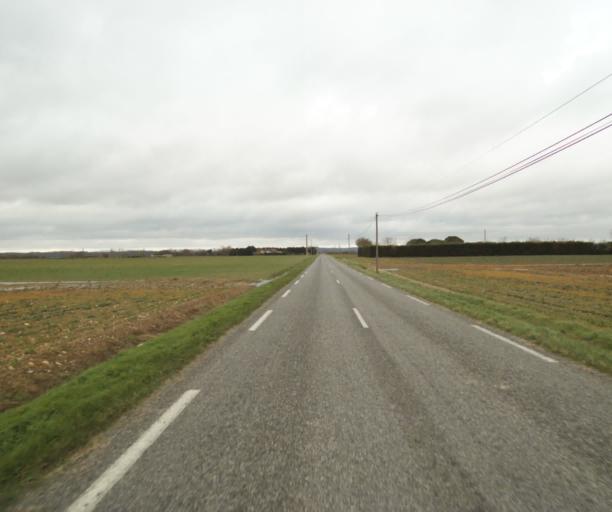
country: FR
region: Midi-Pyrenees
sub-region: Departement de l'Ariege
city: Mazeres
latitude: 43.2288
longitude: 1.6487
